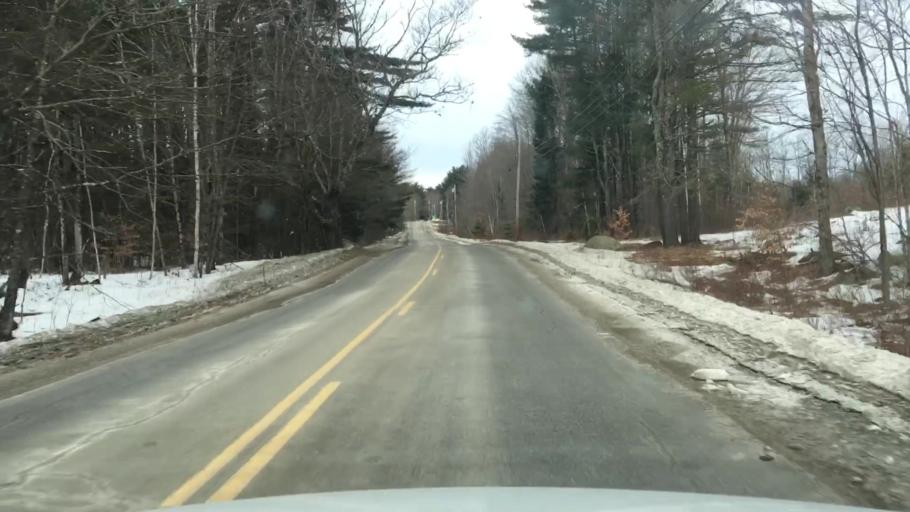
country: US
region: Maine
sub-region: Kennebec County
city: Chelsea
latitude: 44.2677
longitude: -69.6511
